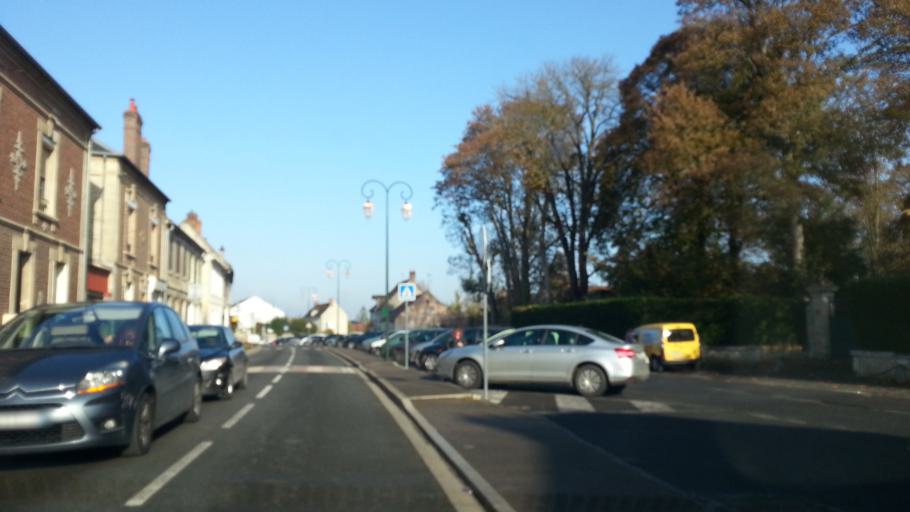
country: FR
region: Picardie
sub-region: Departement de l'Oise
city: Balagny-sur-Therain
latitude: 49.2946
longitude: 2.3366
